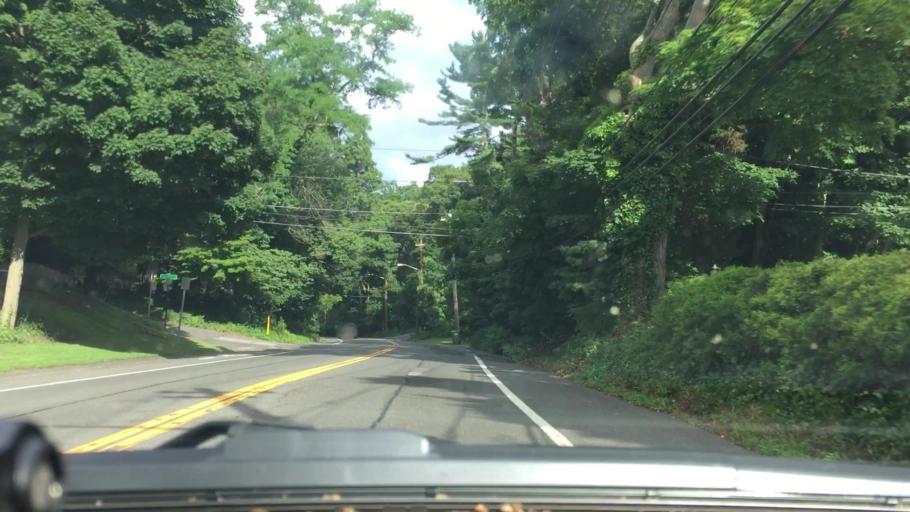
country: US
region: New York
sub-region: Suffolk County
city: Port Jefferson
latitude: 40.9446
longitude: -73.0786
